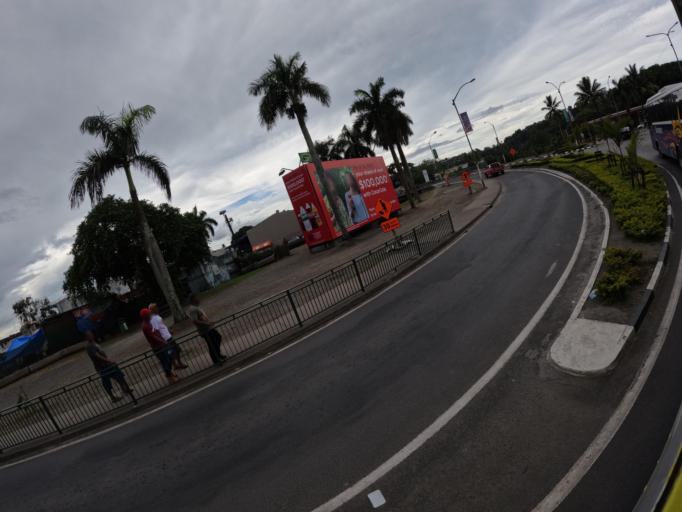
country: FJ
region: Central
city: Suva
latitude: -18.1324
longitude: 178.4270
